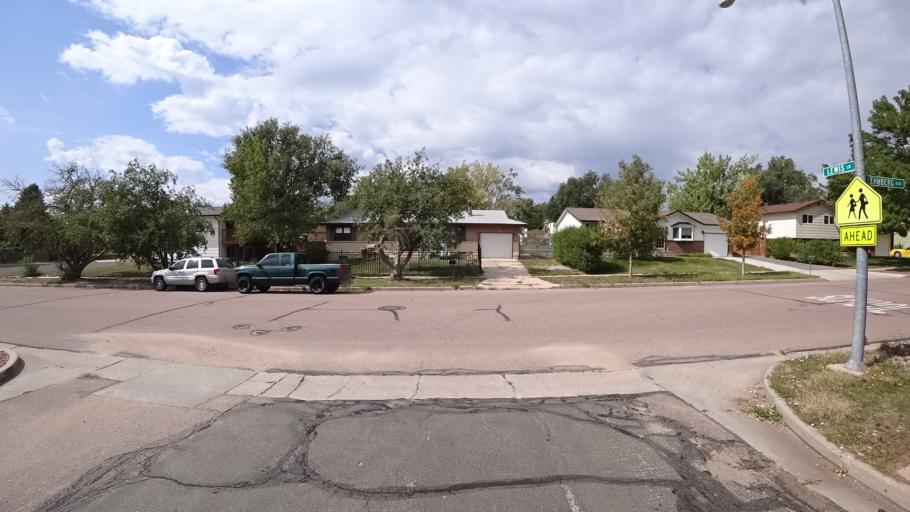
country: US
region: Colorado
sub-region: El Paso County
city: Cimarron Hills
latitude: 38.8497
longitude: -104.7323
